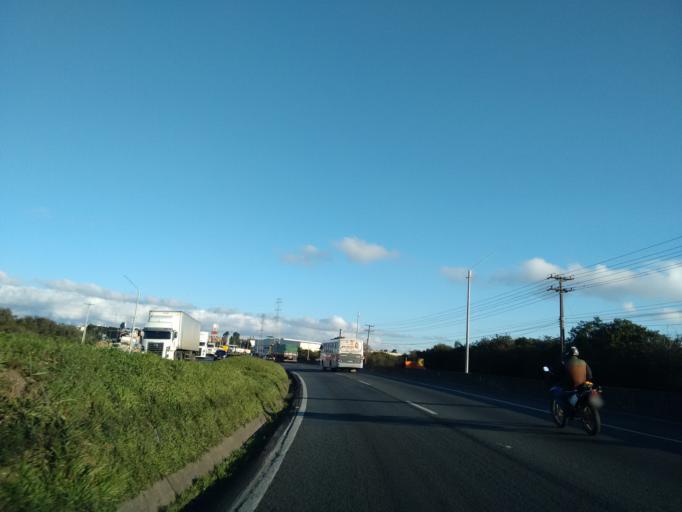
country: BR
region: Parana
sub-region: Sao Jose Dos Pinhais
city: Sao Jose dos Pinhais
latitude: -25.5970
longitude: -49.1739
